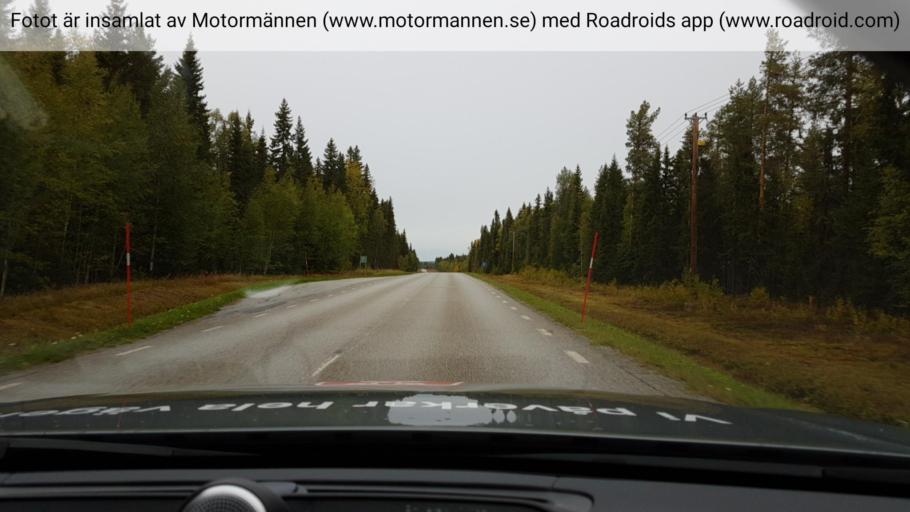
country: SE
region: Jaemtland
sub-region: Stroemsunds Kommun
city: Stroemsund
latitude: 63.9231
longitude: 15.5126
